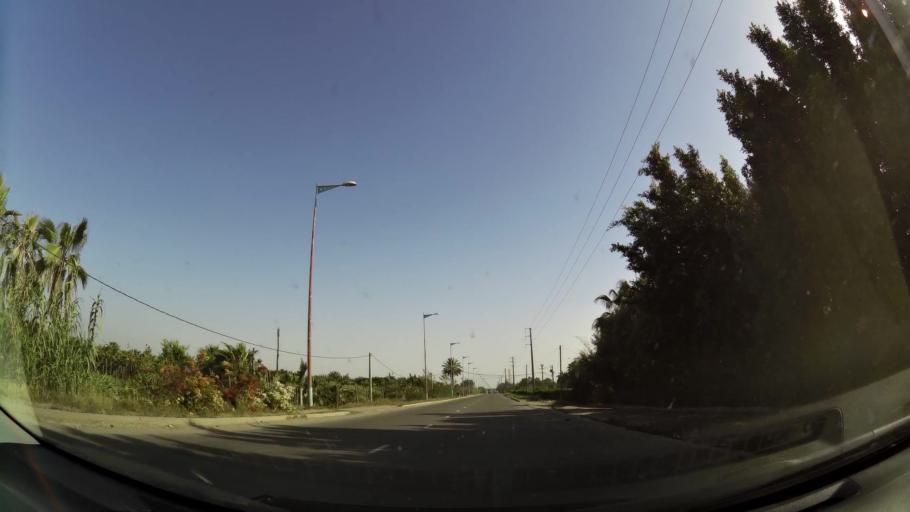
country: MA
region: Souss-Massa-Draa
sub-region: Inezgane-Ait Mellou
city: Inezgane
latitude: 30.3659
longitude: -9.5060
